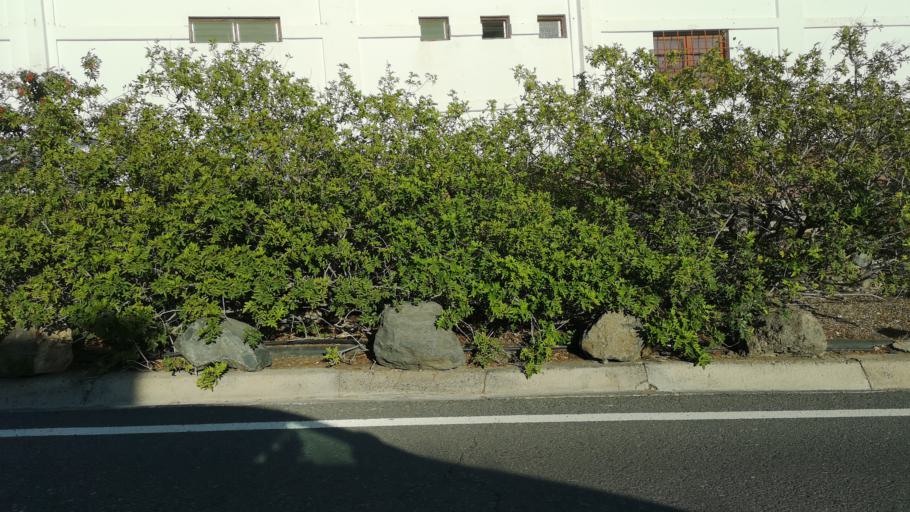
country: ES
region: Canary Islands
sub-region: Provincia de Santa Cruz de Tenerife
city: Alajero
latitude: 28.0323
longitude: -17.1907
